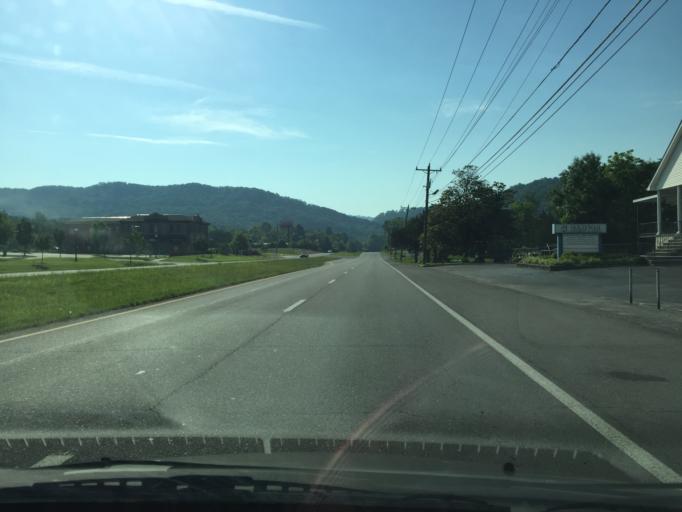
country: US
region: Tennessee
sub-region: Hamilton County
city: Collegedale
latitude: 35.0820
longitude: -85.0567
